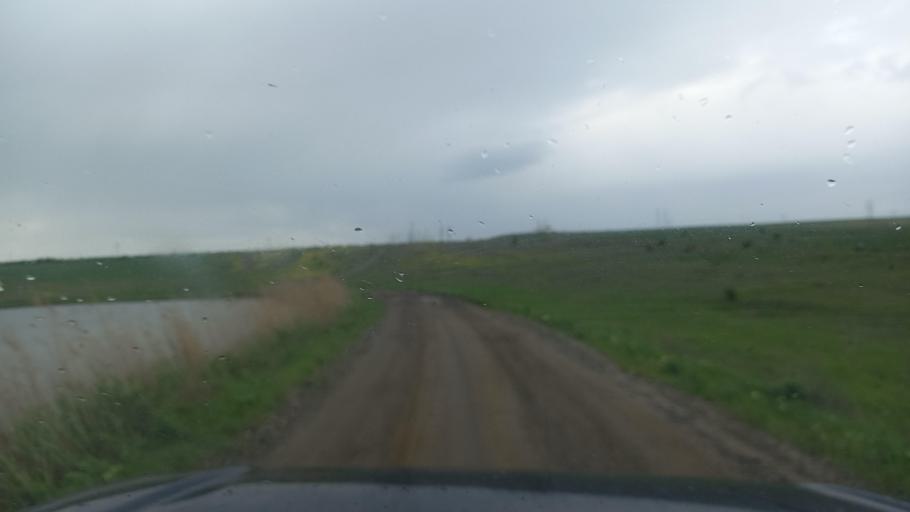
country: RU
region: Stavropol'skiy
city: Nevinnomyssk
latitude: 44.6005
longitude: 42.2373
